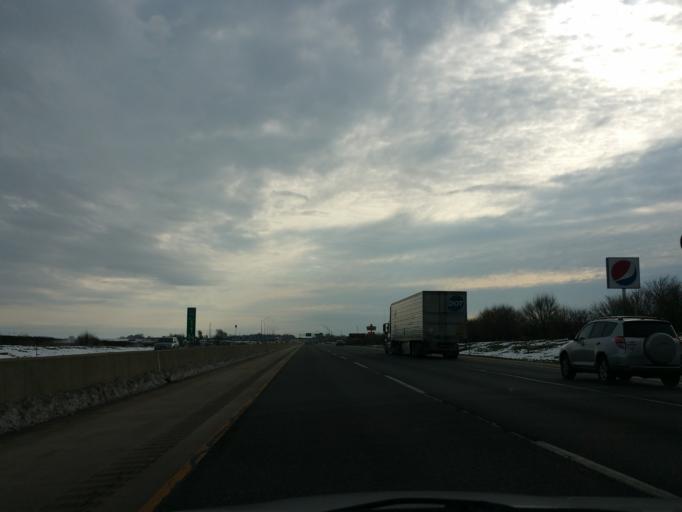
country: US
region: Illinois
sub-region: Winnebago County
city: Machesney Park
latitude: 42.3297
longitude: -88.9646
